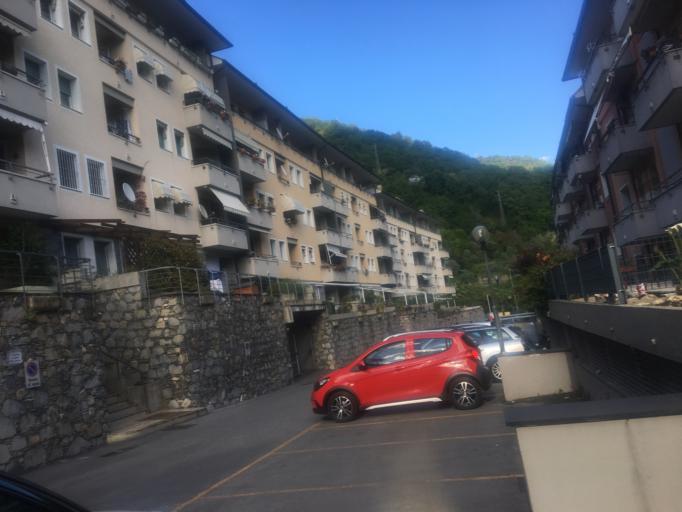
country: IT
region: Liguria
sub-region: Provincia di Genova
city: Piccarello
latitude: 44.4556
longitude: 8.9838
